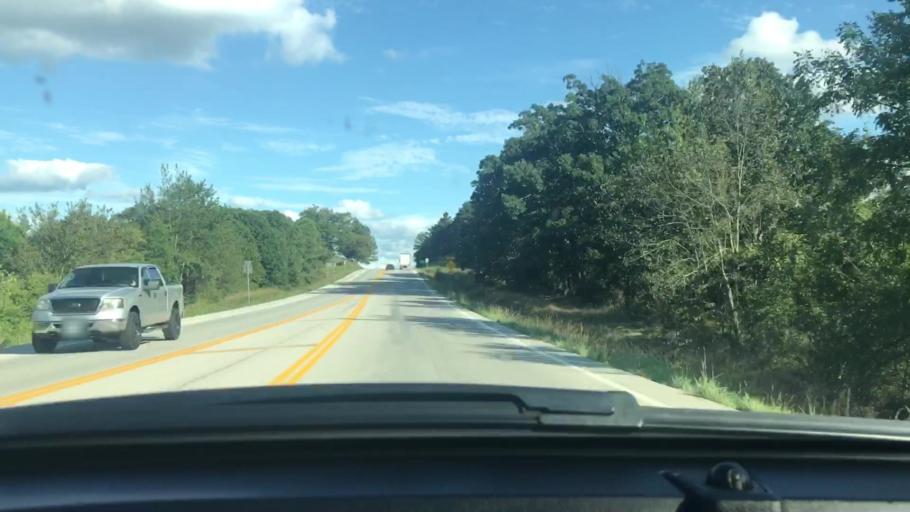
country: US
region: Missouri
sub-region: Howell County
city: West Plains
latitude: 36.6510
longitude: -91.6890
